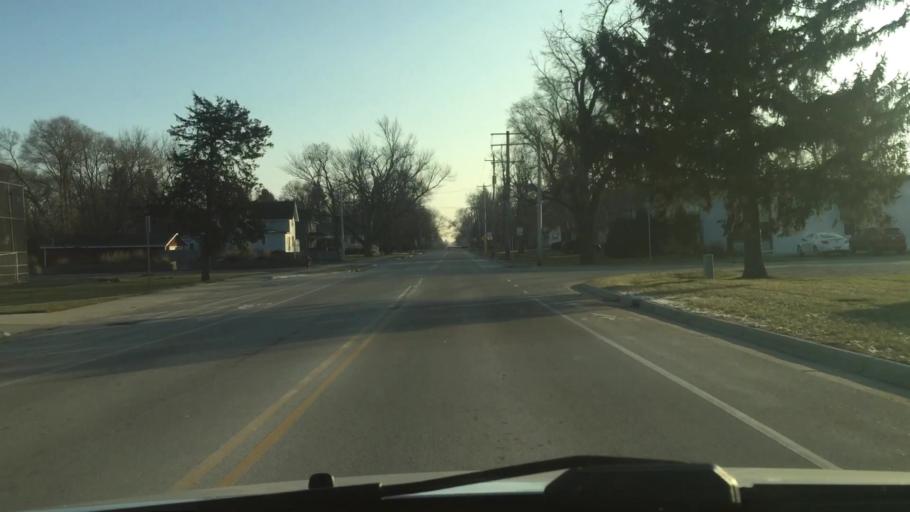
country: US
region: Wisconsin
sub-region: Waukesha County
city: Dousman
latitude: 43.0127
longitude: -88.4729
